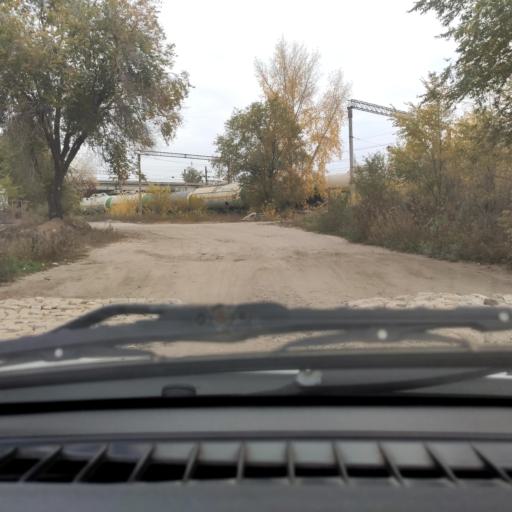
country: RU
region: Samara
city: Zhigulevsk
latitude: 53.4862
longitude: 49.4994
